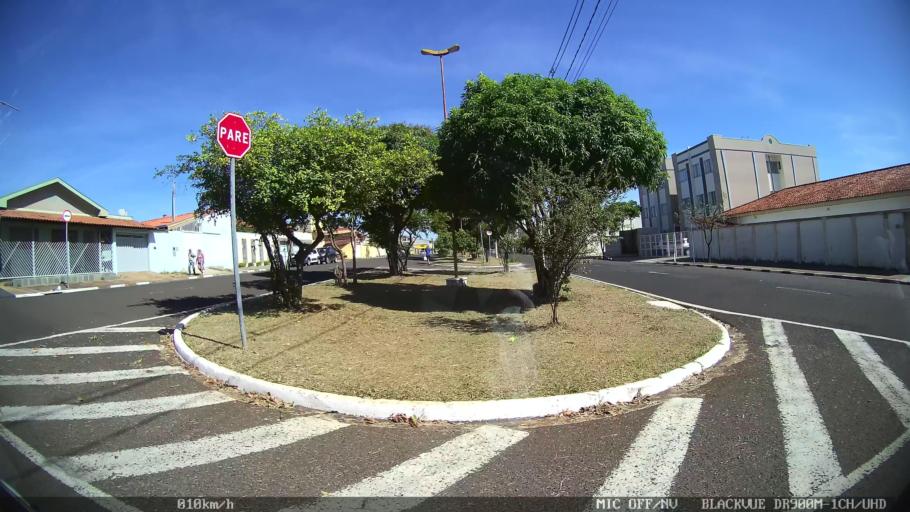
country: BR
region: Sao Paulo
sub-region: Franca
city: Franca
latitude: -20.5578
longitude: -47.3996
